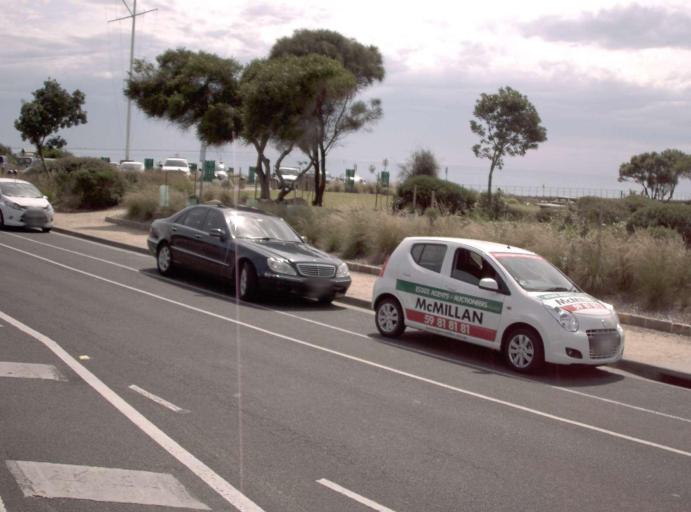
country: AU
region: Victoria
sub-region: Mornington Peninsula
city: Dromana
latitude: -38.3322
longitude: 144.9660
